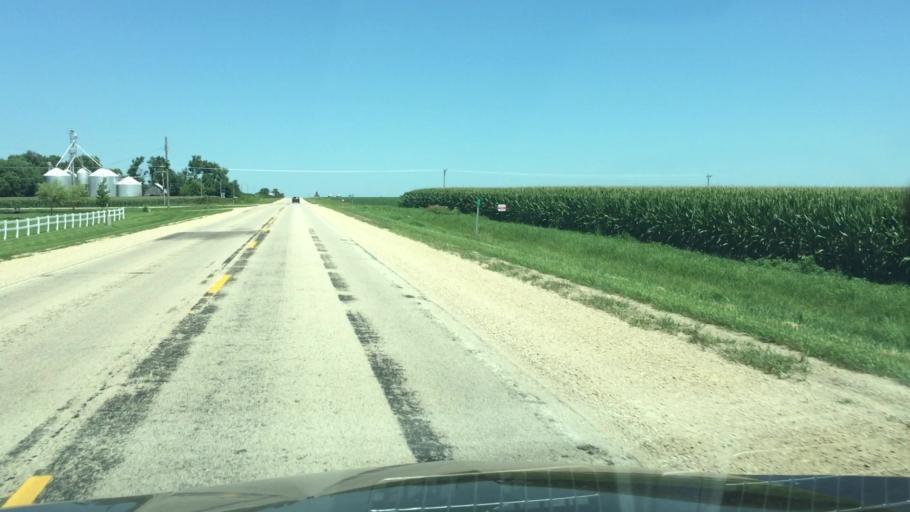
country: US
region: Iowa
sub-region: Cedar County
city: Mechanicsville
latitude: 41.9160
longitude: -91.1519
